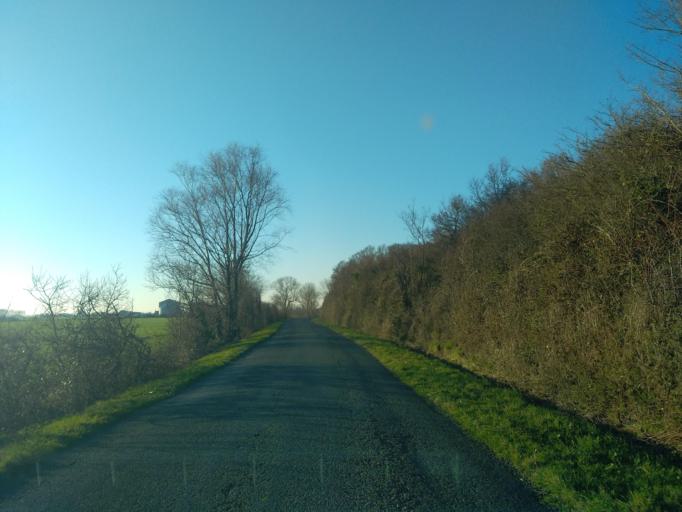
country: FR
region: Pays de la Loire
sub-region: Departement de la Vendee
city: Triaize
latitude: 46.3933
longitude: -1.2924
